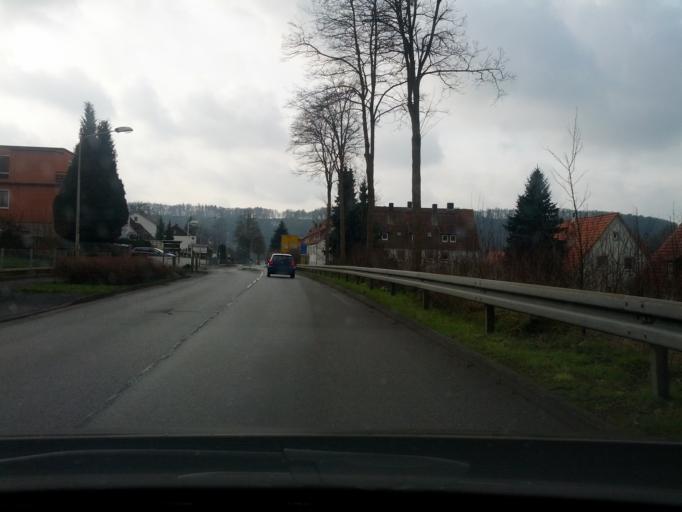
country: DE
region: Lower Saxony
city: Bad Karlshafen
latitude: 51.6489
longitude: 9.4603
